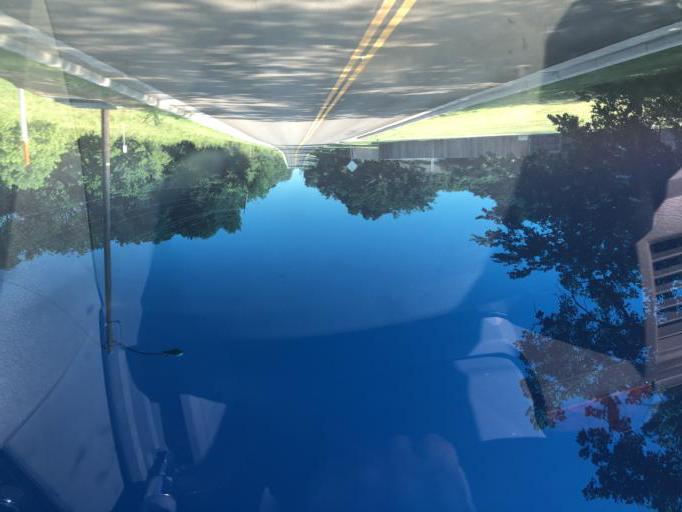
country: US
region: Texas
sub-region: Dallas County
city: Grand Prairie
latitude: 32.7201
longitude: -97.0197
